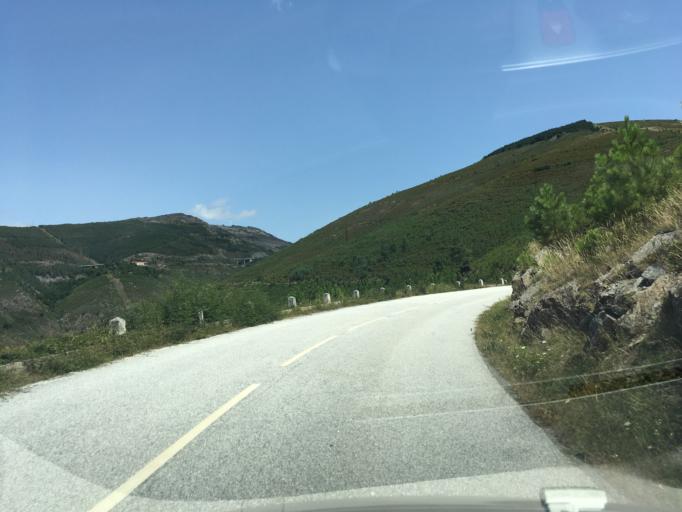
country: PT
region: Vila Real
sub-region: Mesao Frio
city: Mesao Frio
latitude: 41.2620
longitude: -7.9369
